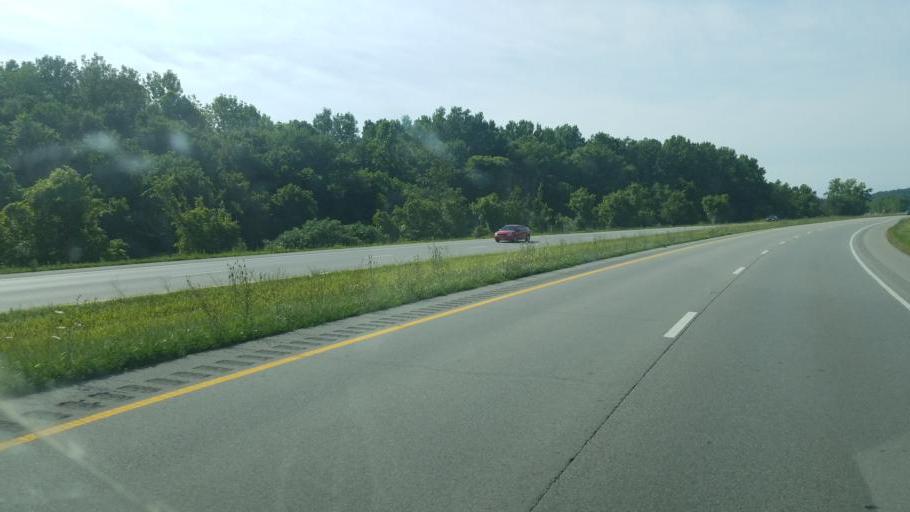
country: US
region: Ohio
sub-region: Hocking County
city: Logan
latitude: 39.5050
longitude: -82.3560
